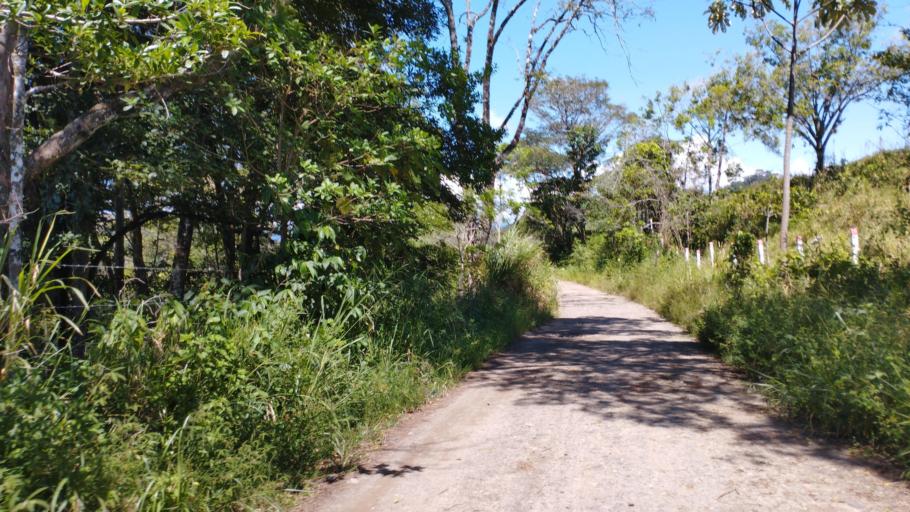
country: CO
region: Boyaca
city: San Luis de Gaceno
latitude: 4.7914
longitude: -73.1067
